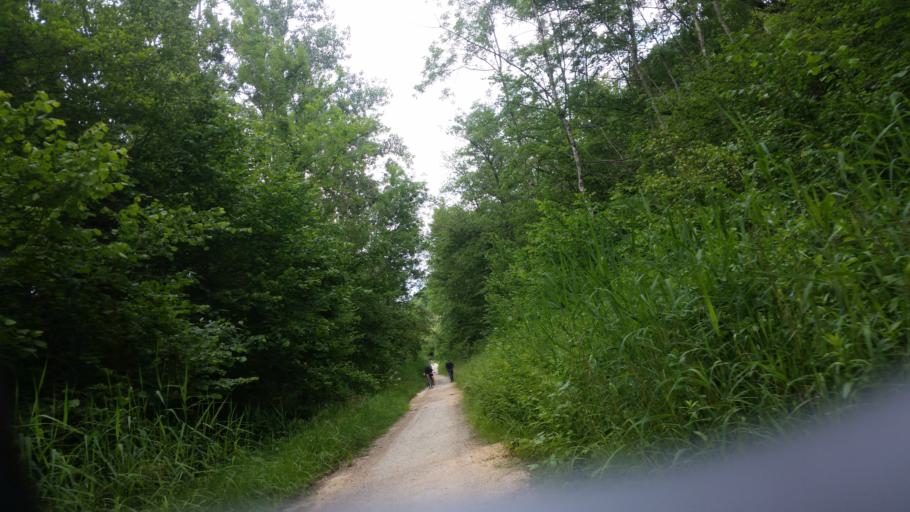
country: CH
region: Fribourg
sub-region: Broye District
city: Estavayer-le-Lac
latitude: 46.8276
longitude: 6.8027
